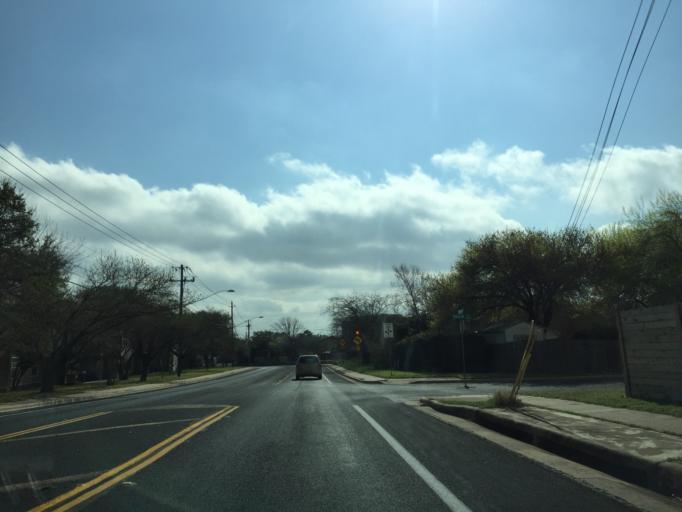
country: US
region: Texas
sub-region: Williamson County
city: Jollyville
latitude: 30.4123
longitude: -97.7312
